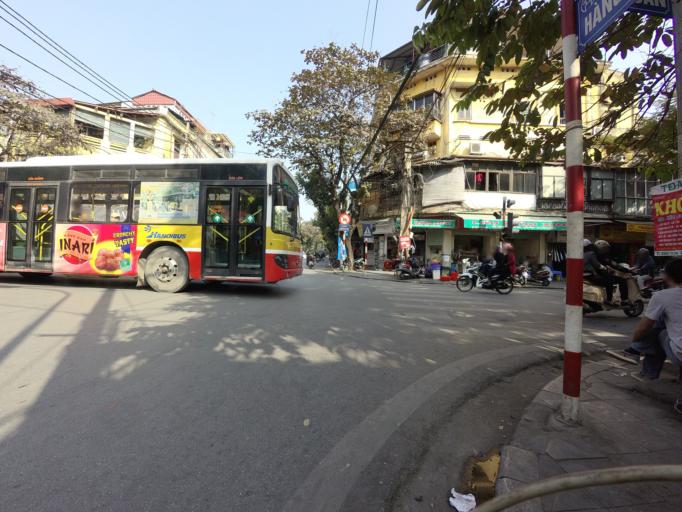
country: VN
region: Ha Noi
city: Hoan Kiem
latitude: 21.0304
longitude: 105.8474
